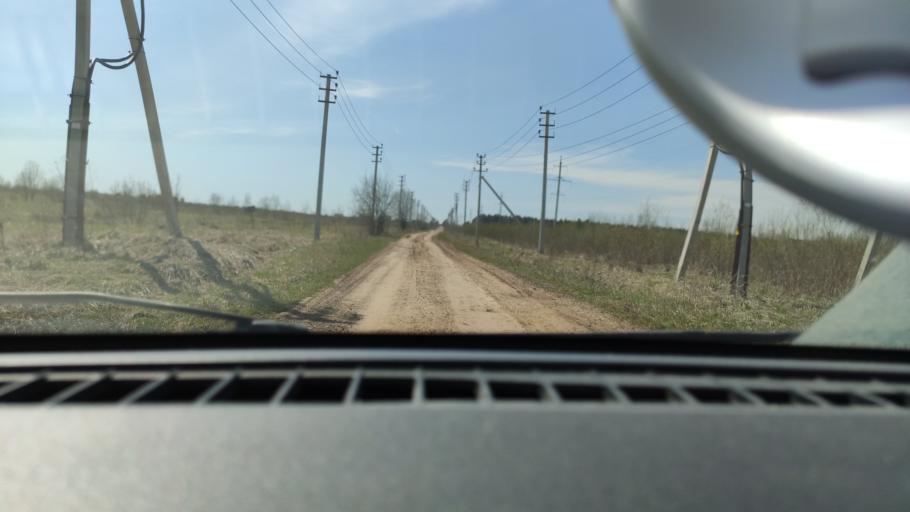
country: RU
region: Perm
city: Kultayevo
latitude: 57.8917
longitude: 55.8665
